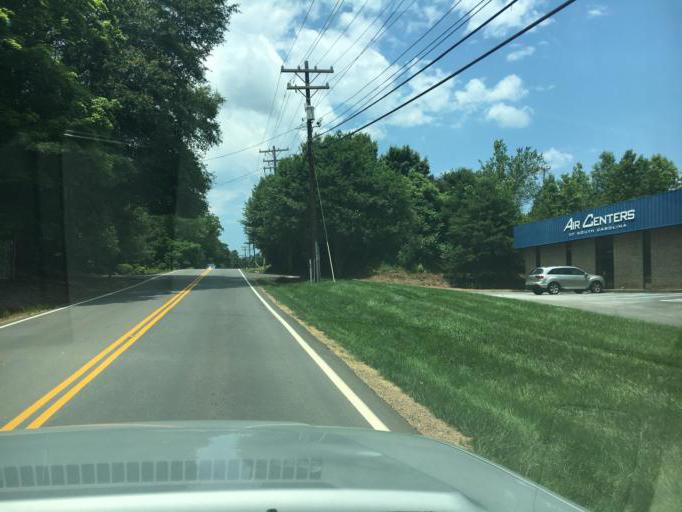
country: US
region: South Carolina
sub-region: Greenville County
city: Five Forks
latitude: 34.8608
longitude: -82.2361
